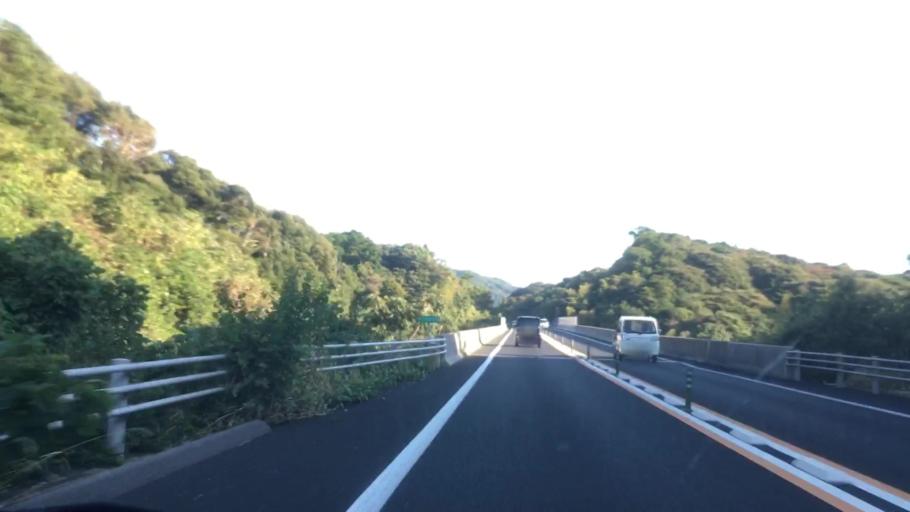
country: JP
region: Nagasaki
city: Sasebo
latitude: 33.1965
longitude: 129.6781
